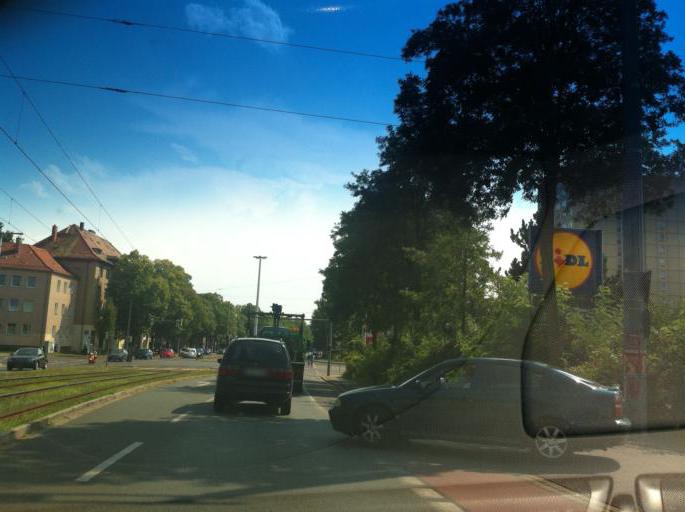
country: DE
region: Saxony
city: Leipzig
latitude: 51.3109
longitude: 12.3958
